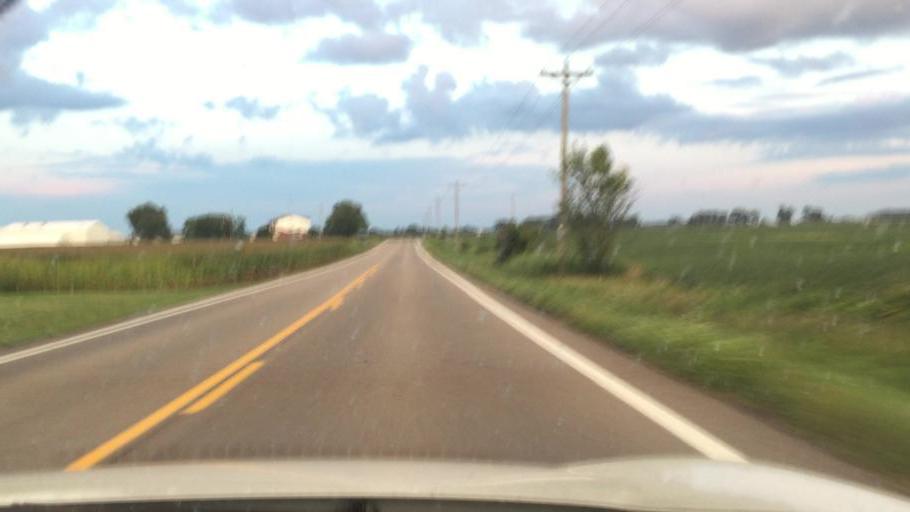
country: US
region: Ohio
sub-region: Champaign County
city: Mechanicsburg
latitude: 40.0473
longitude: -83.5187
